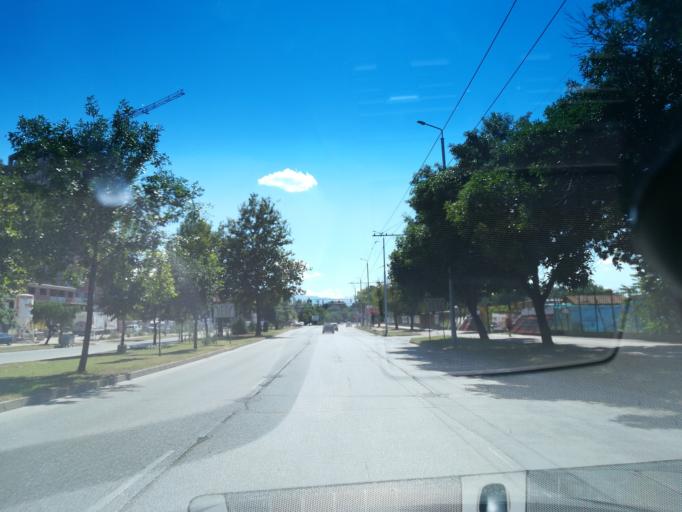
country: BG
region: Plovdiv
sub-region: Obshtina Plovdiv
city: Plovdiv
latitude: 42.1283
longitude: 24.7719
